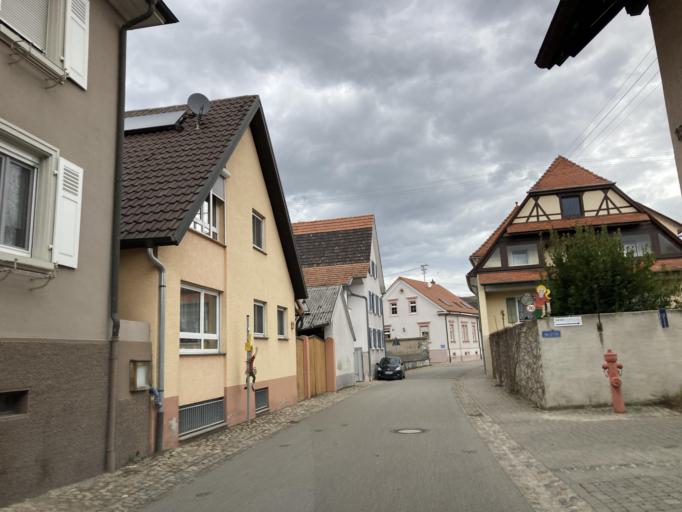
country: DE
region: Baden-Wuerttemberg
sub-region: Freiburg Region
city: Vogtsburg
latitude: 48.1038
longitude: 7.6272
